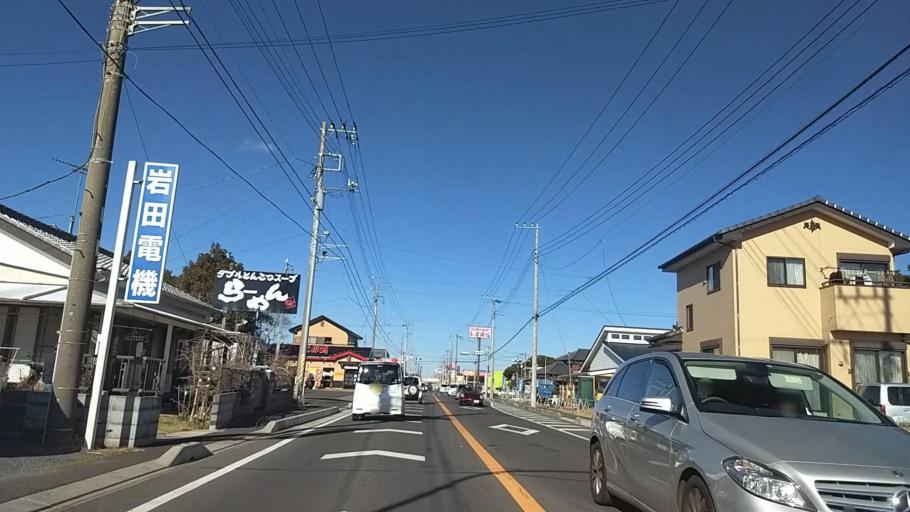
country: JP
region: Chiba
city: Ohara
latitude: 35.2605
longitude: 140.3935
